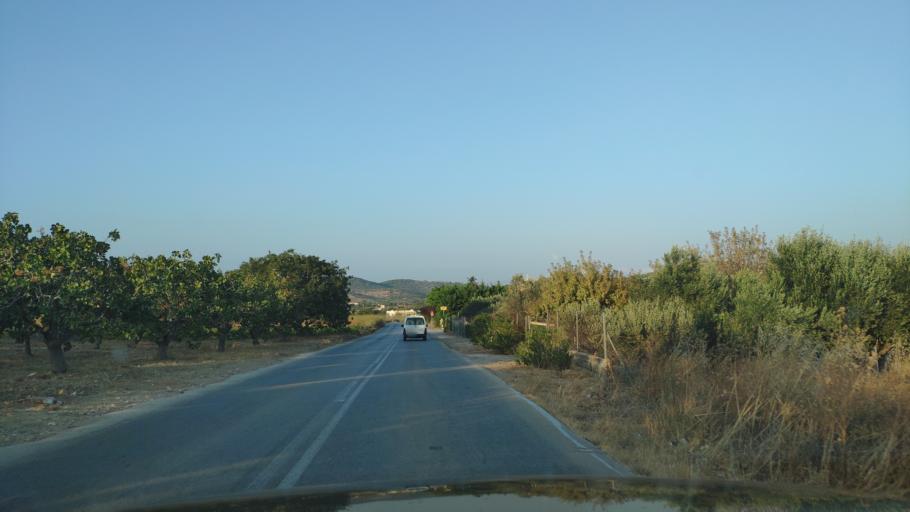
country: GR
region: Attica
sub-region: Nomarchia Anatolikis Attikis
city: Markopoulo
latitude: 37.9093
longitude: 23.9639
